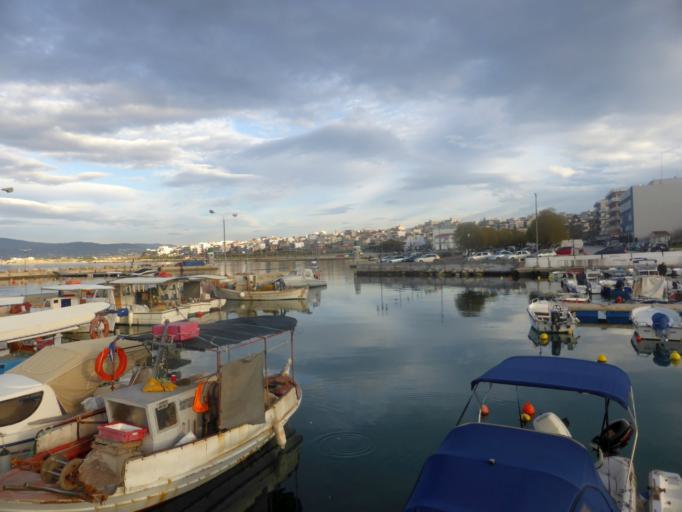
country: GR
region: Peloponnese
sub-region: Nomos Korinthias
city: Korinthos
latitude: 37.9412
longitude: 22.9348
